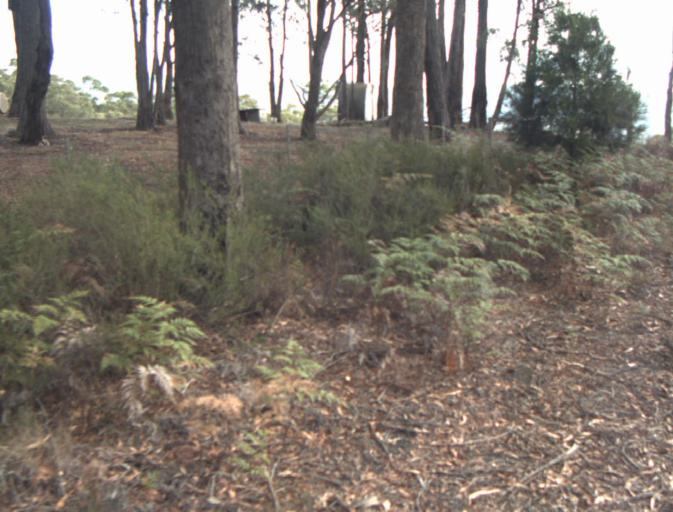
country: AU
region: Tasmania
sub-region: Launceston
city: Mayfield
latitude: -41.2163
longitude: 147.1769
